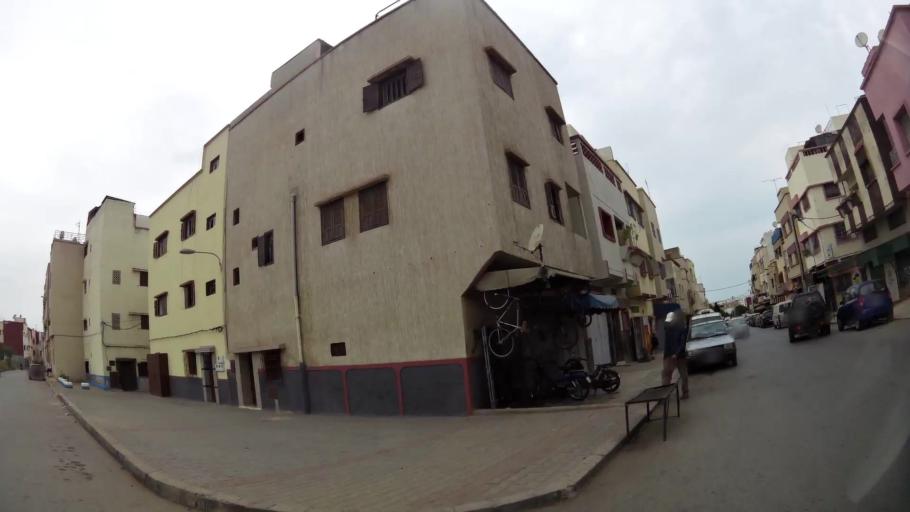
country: MA
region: Rabat-Sale-Zemmour-Zaer
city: Sale
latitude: 34.0312
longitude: -6.8058
